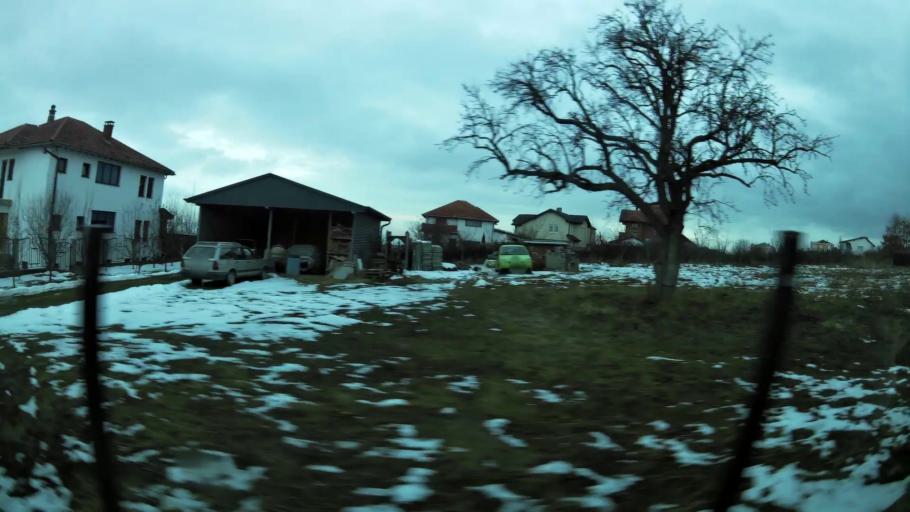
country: XK
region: Pristina
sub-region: Komuna e Prishtines
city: Pristina
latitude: 42.6249
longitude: 21.1649
